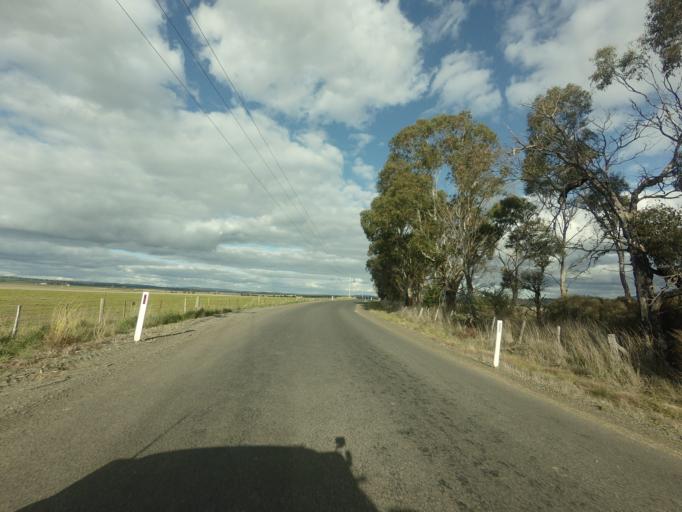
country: AU
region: Tasmania
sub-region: Northern Midlands
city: Longford
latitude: -41.8072
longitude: 147.1823
